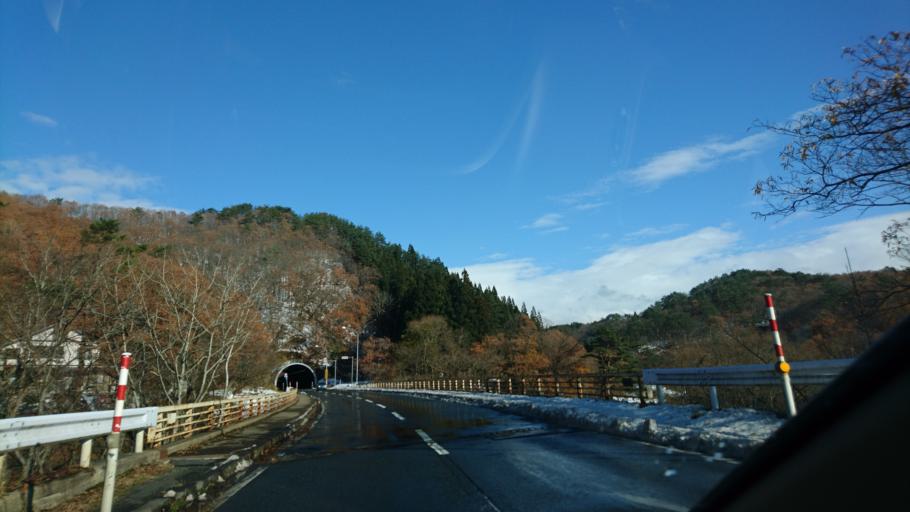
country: JP
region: Akita
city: Yokotemachi
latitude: 39.3107
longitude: 140.7640
